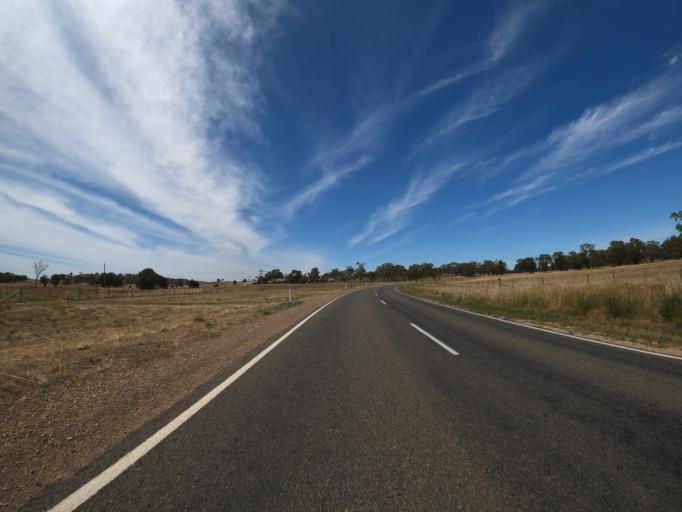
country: AU
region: Victoria
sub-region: Benalla
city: Benalla
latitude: -36.3292
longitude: 145.9615
